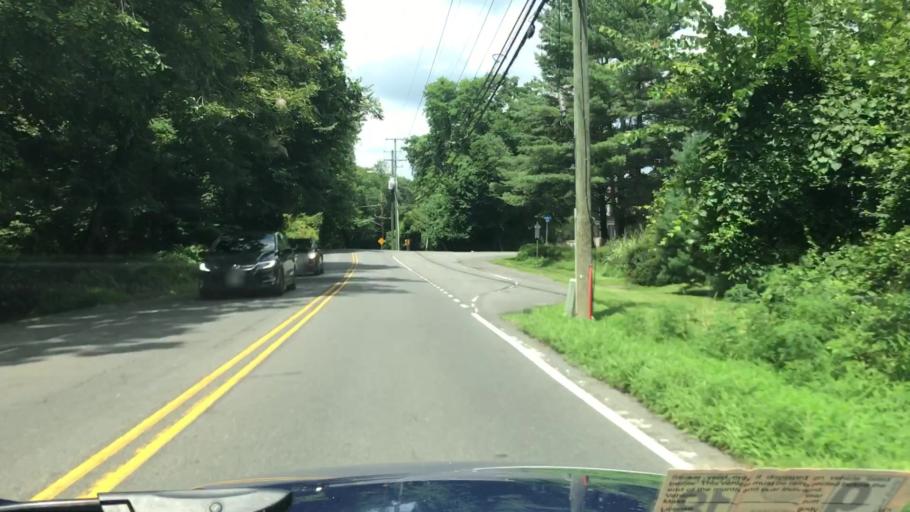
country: US
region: Virginia
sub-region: Fairfax County
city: Vienna
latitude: 38.9093
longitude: -77.2837
